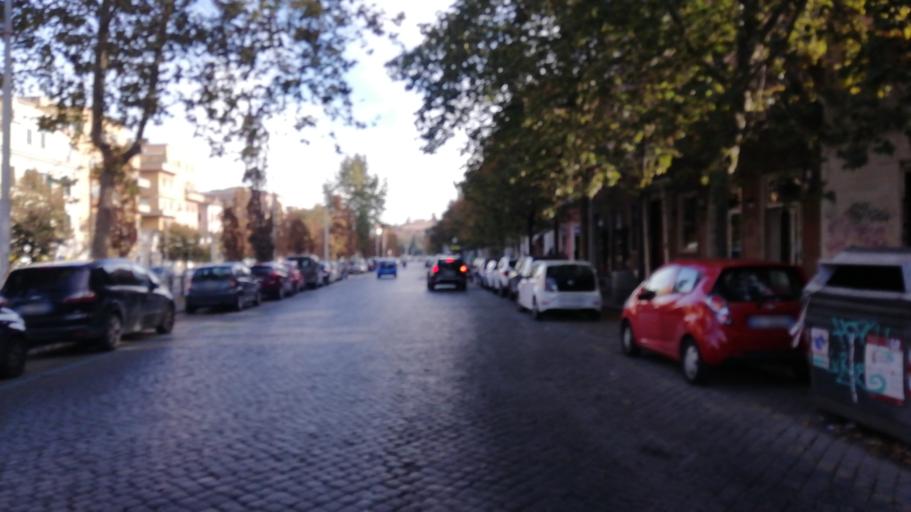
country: IT
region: Latium
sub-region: Citta metropolitana di Roma Capitale
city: Rome
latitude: 41.8809
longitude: 12.4849
